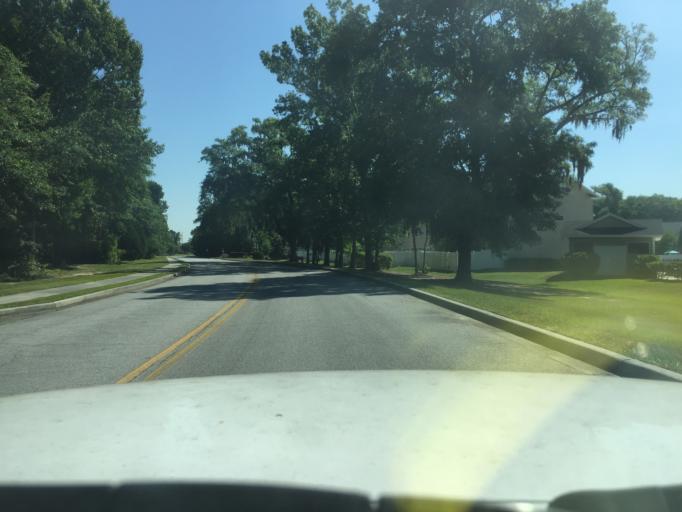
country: US
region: Georgia
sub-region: Chatham County
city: Georgetown
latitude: 32.0024
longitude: -81.2586
